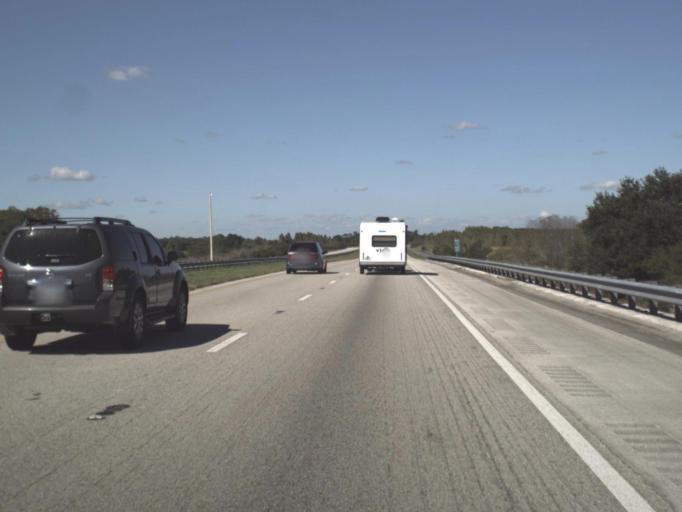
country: US
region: Florida
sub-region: Osceola County
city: Saint Cloud
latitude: 28.0087
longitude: -81.1595
